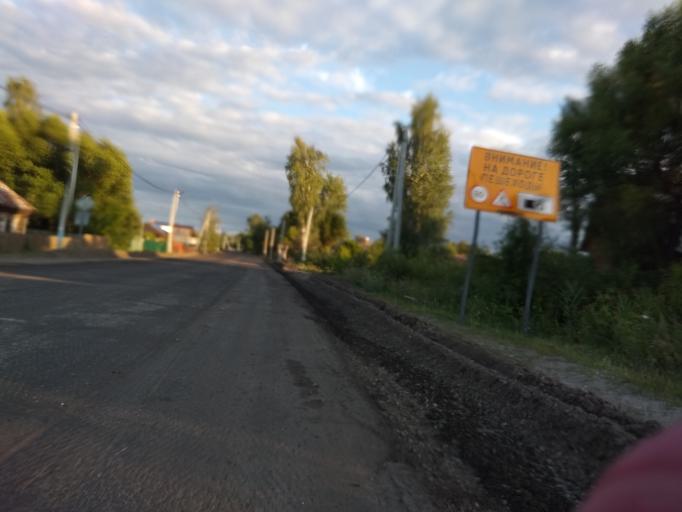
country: RU
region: Moskovskaya
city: Misheronskiy
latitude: 55.6568
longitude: 39.7519
